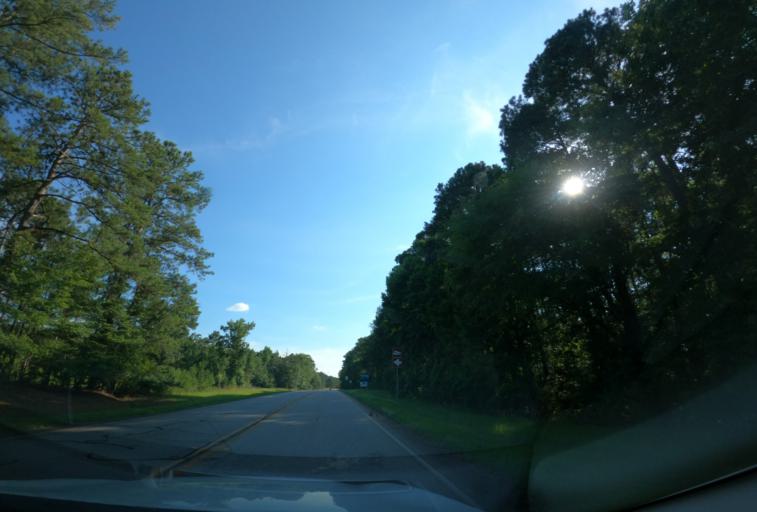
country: US
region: Georgia
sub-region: Lincoln County
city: Lincolnton
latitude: 33.8517
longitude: -82.3949
